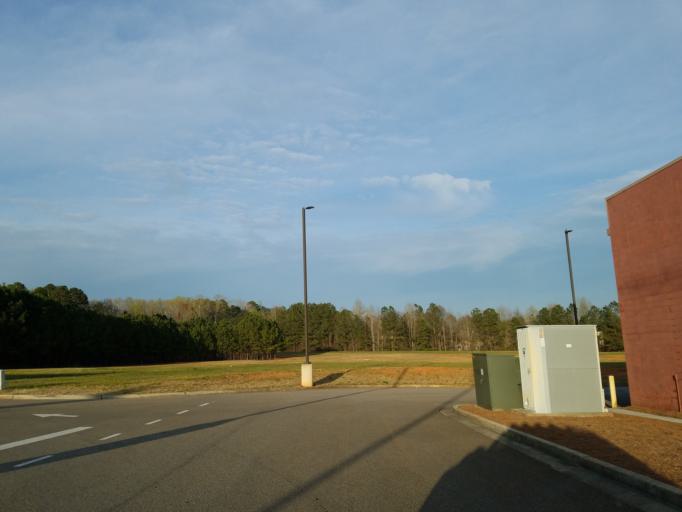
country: US
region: Georgia
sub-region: Dawson County
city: Dawsonville
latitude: 34.4179
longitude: -84.1117
